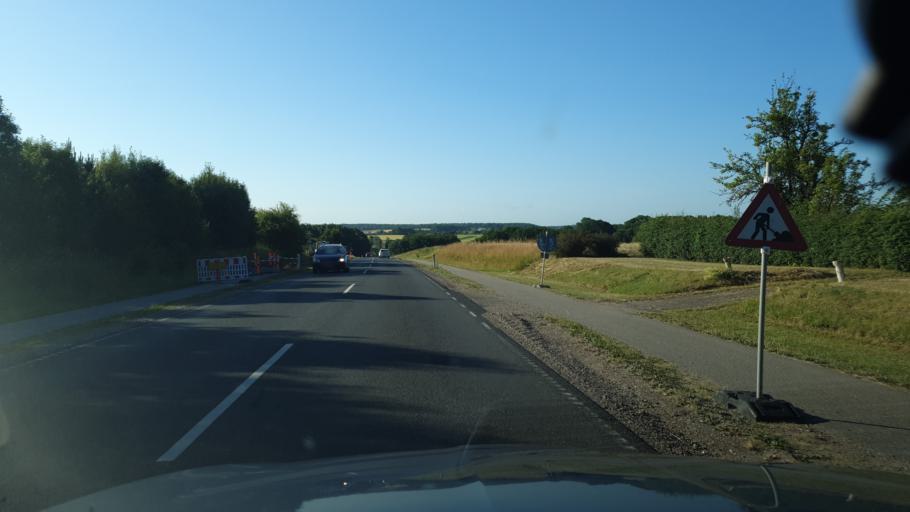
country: DK
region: Zealand
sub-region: Soro Kommune
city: Frederiksberg
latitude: 55.3924
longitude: 11.6405
